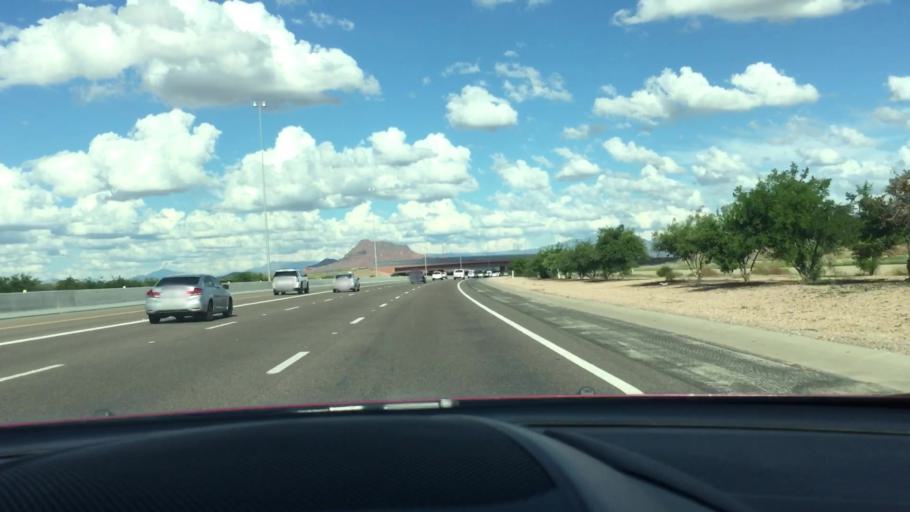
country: US
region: Arizona
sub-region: Maricopa County
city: Mesa
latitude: 33.4781
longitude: -111.7739
